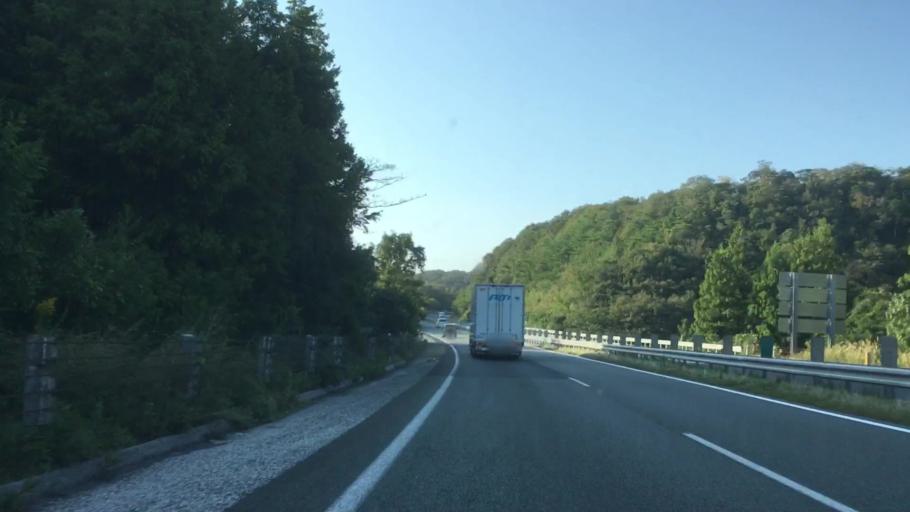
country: JP
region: Yamaguchi
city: Ogori-shimogo
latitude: 34.1601
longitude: 131.3303
